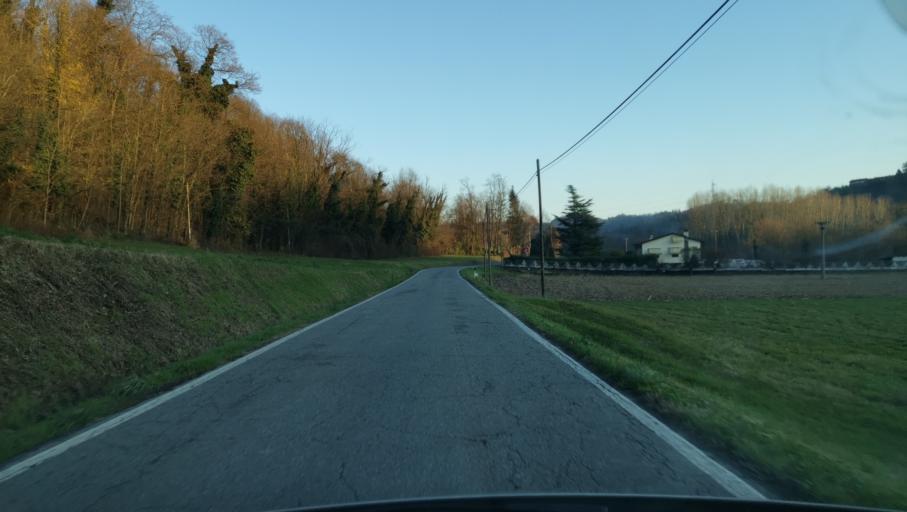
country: IT
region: Piedmont
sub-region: Provincia di Torino
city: Rivalba
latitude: 45.1158
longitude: 7.8712
